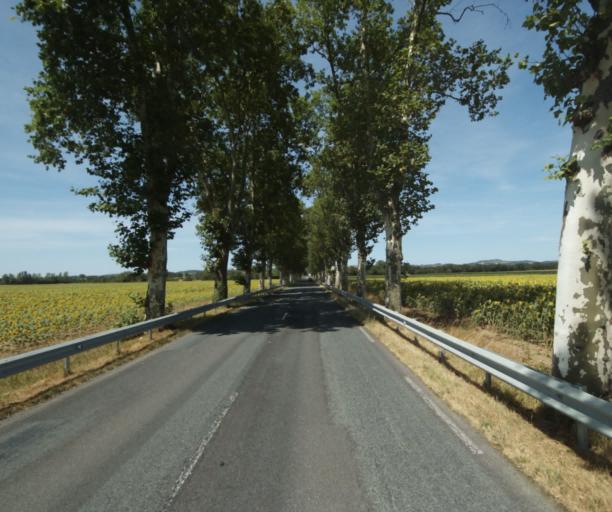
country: FR
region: Midi-Pyrenees
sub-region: Departement de la Haute-Garonne
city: Revel
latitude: 43.5078
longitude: 2.0110
